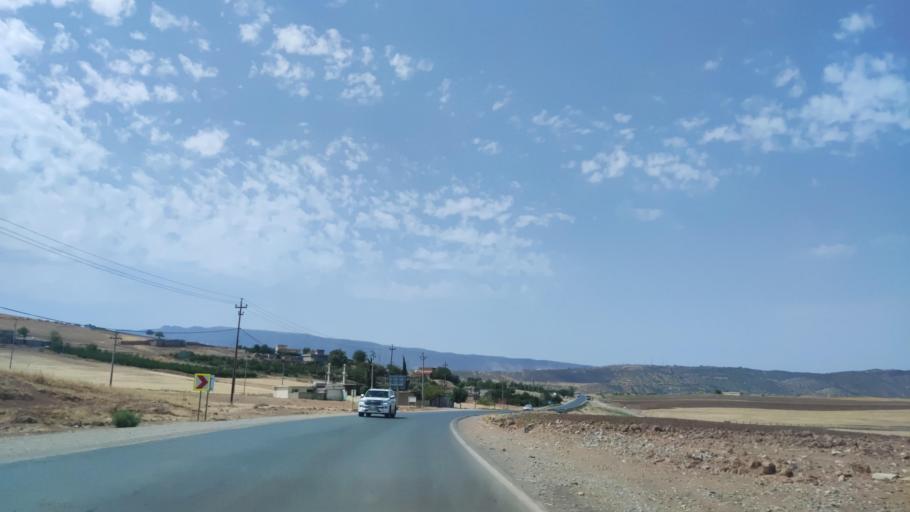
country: IQ
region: Arbil
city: Shaqlawah
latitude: 36.4666
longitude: 44.3966
